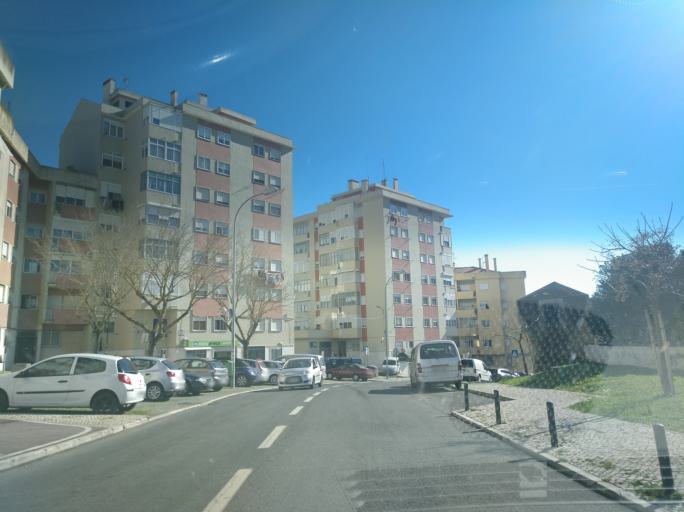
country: PT
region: Lisbon
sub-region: Amadora
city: Amadora
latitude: 38.7576
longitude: -9.2260
